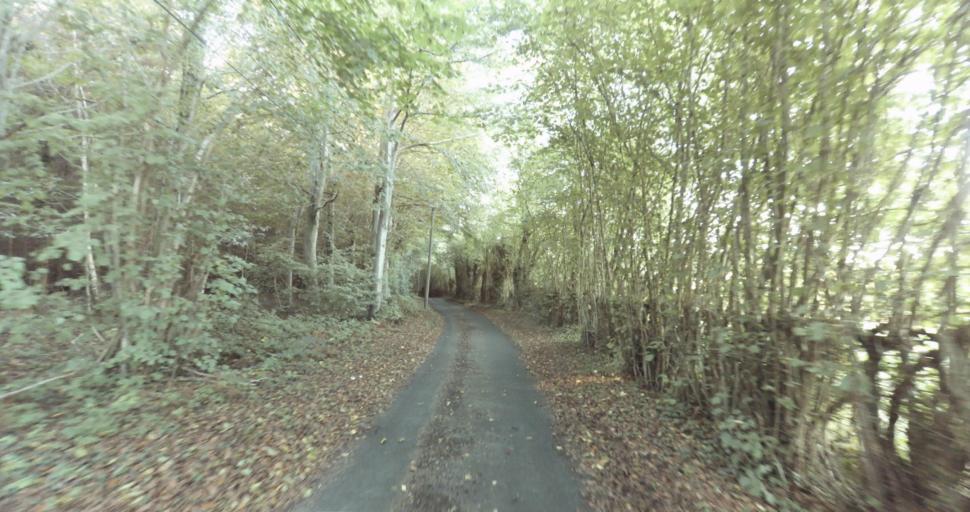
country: FR
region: Lower Normandy
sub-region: Departement de l'Orne
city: Vimoutiers
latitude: 48.8913
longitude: 0.1186
